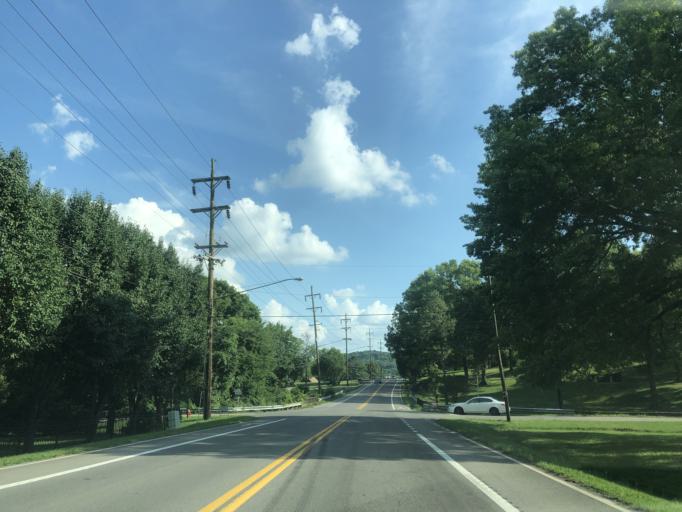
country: US
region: Tennessee
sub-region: Davidson County
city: Nashville
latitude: 36.2385
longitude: -86.8308
